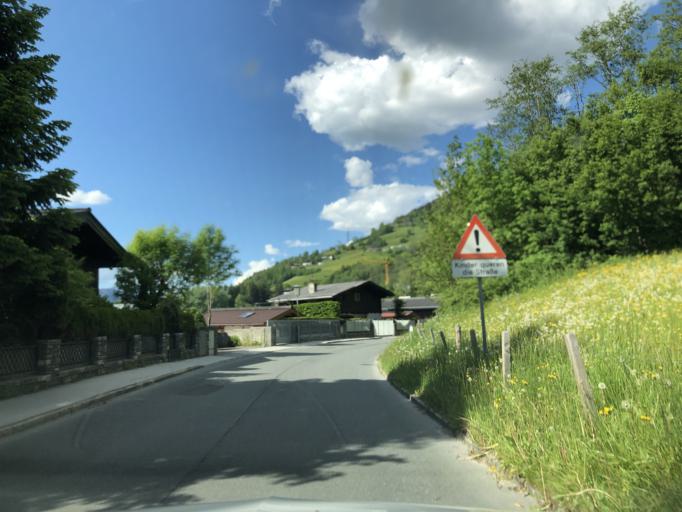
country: AT
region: Salzburg
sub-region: Politischer Bezirk Zell am See
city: Bruck an der Grossglocknerstrasse
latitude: 47.3076
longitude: 12.8160
